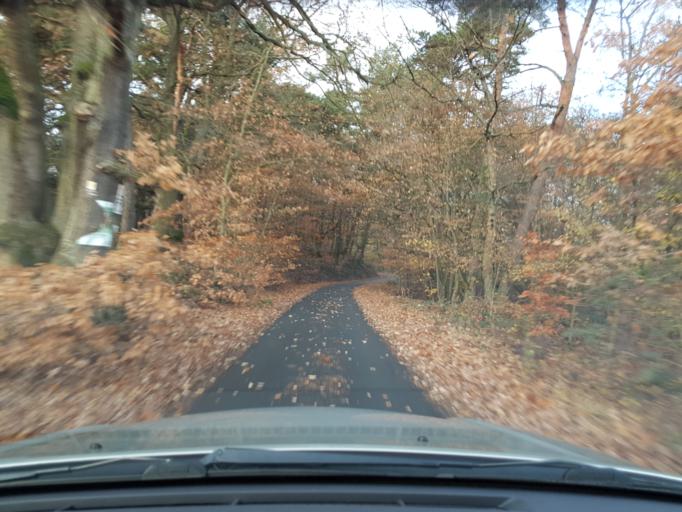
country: DE
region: Hesse
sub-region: Regierungsbezirk Darmstadt
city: Kiedrich
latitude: 50.0374
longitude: 8.0507
